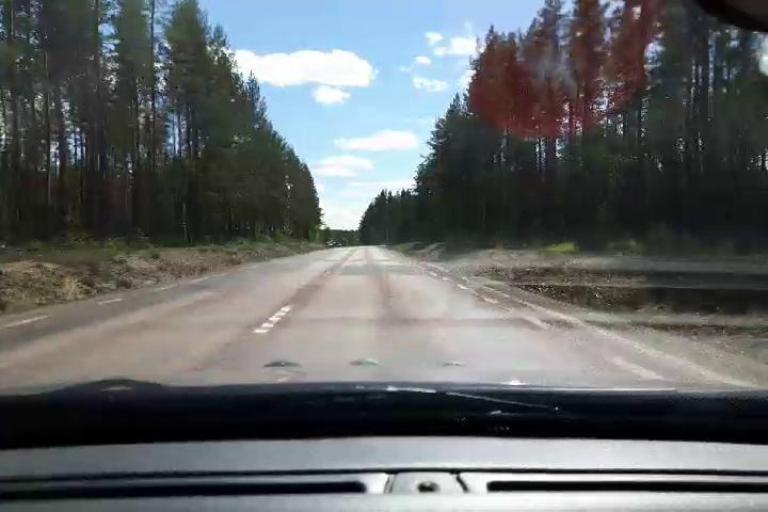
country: SE
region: Gaevleborg
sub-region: Ljusdals Kommun
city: Farila
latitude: 61.8443
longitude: 15.7509
